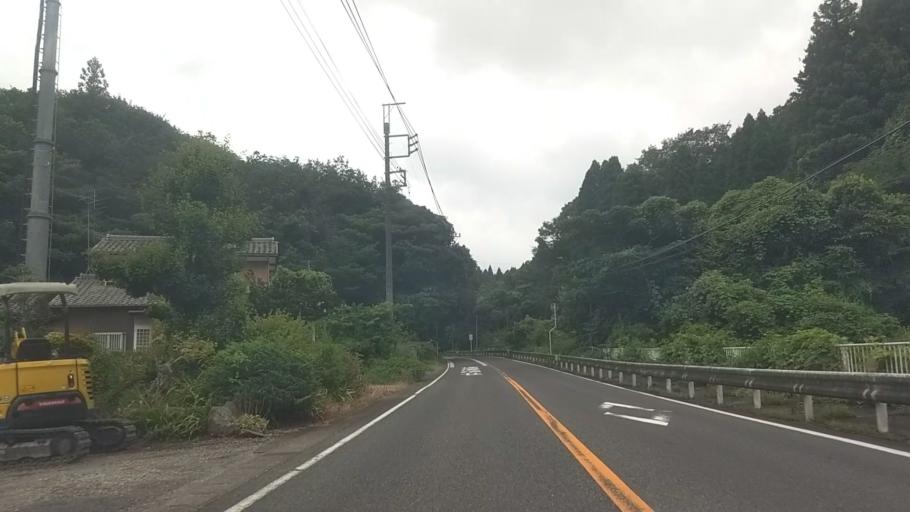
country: JP
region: Chiba
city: Kawaguchi
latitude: 35.2548
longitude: 140.0656
